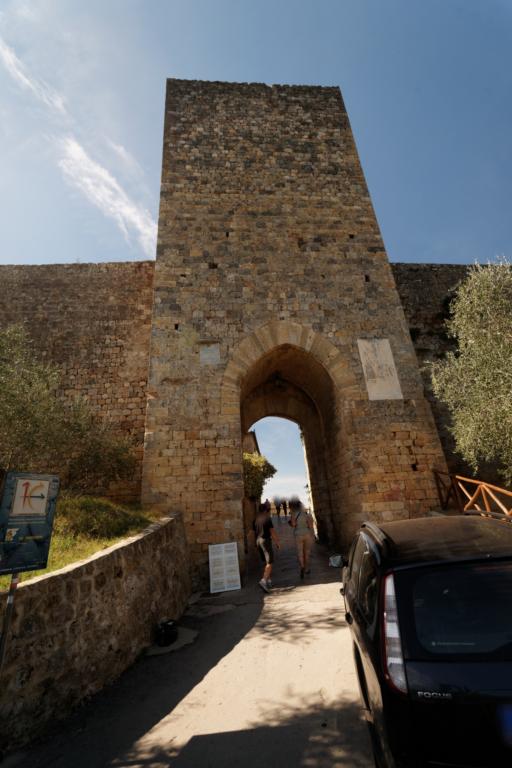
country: IT
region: Tuscany
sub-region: Provincia di Siena
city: Monteriggioni
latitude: 43.3898
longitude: 11.2244
